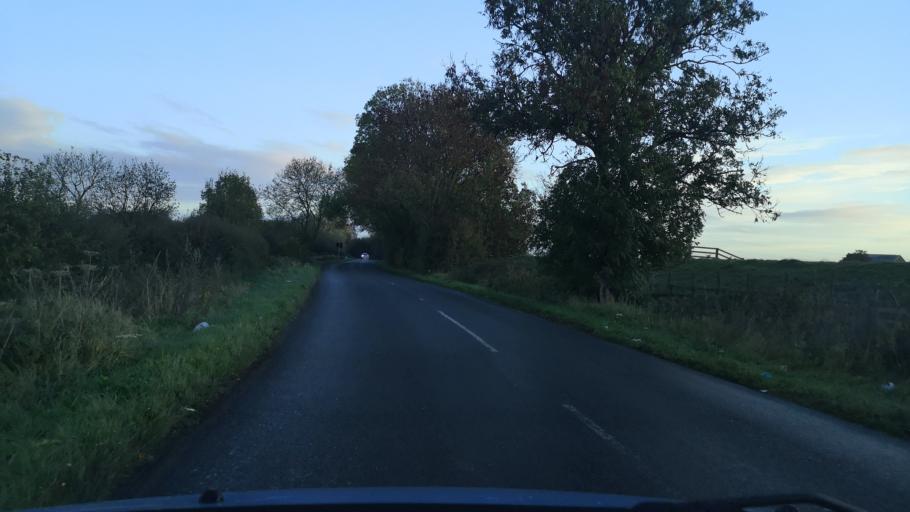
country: GB
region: England
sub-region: Doncaster
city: Hatfield
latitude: 53.6217
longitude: -0.9838
